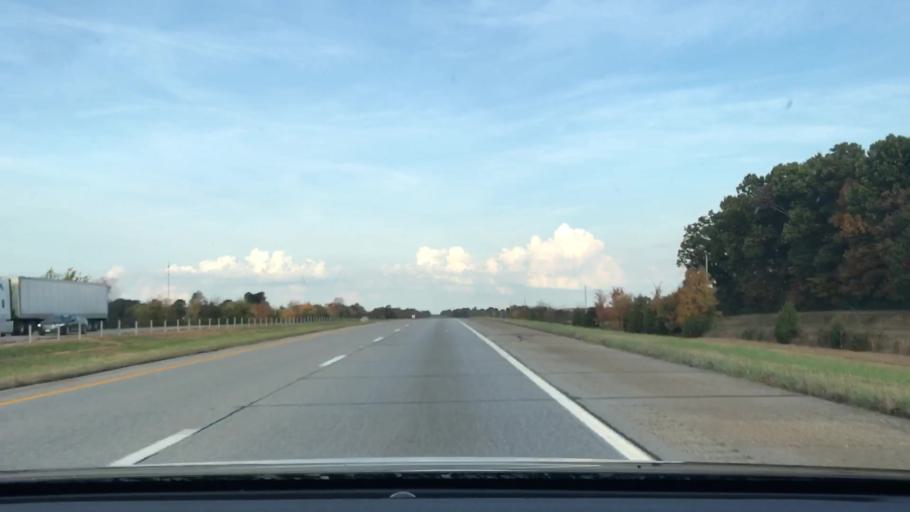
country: US
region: Kentucky
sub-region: Caldwell County
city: Princeton
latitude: 36.9855
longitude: -87.9242
